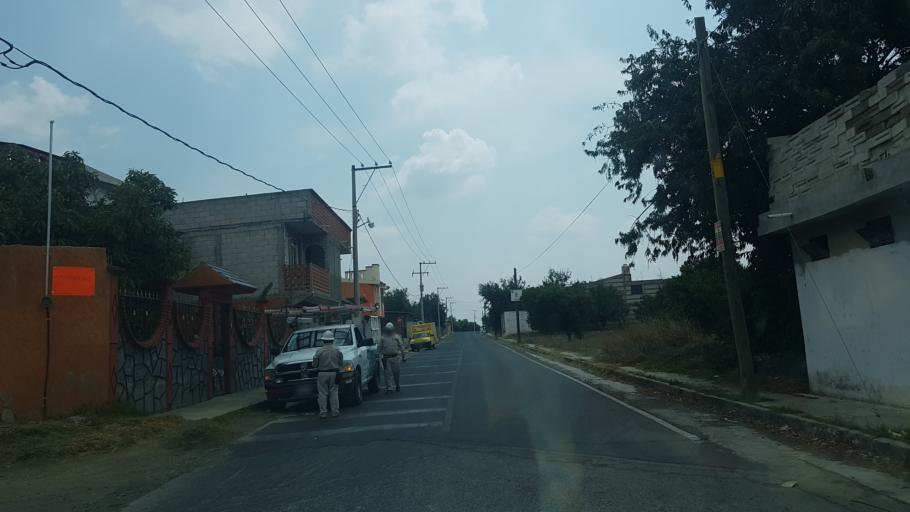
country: MX
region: Puebla
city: Domingo Arenas
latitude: 19.1411
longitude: -98.4692
